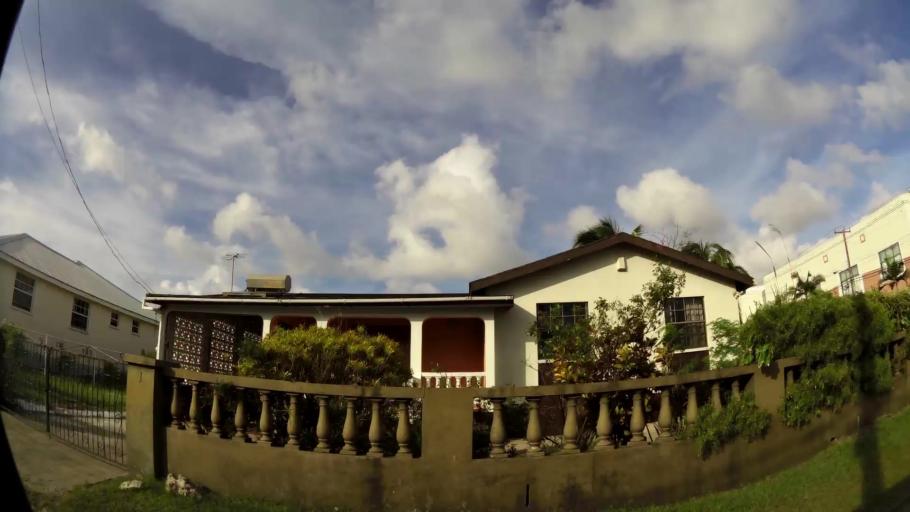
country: BB
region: Christ Church
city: Oistins
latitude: 13.0833
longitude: -59.5682
